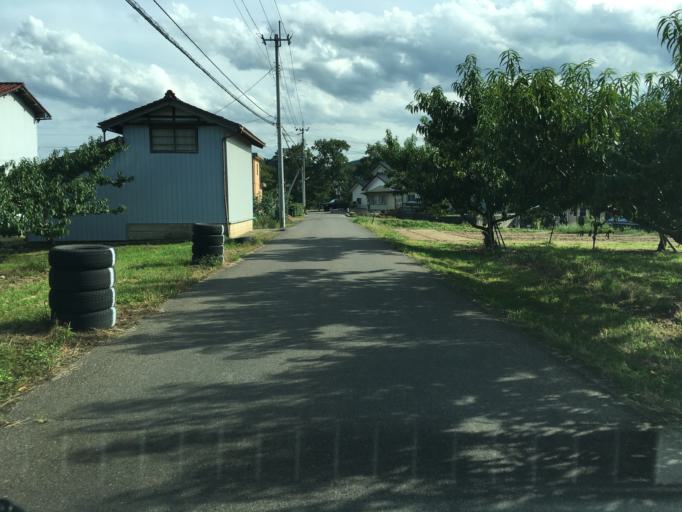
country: JP
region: Fukushima
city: Hobaramachi
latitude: 37.8171
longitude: 140.5238
